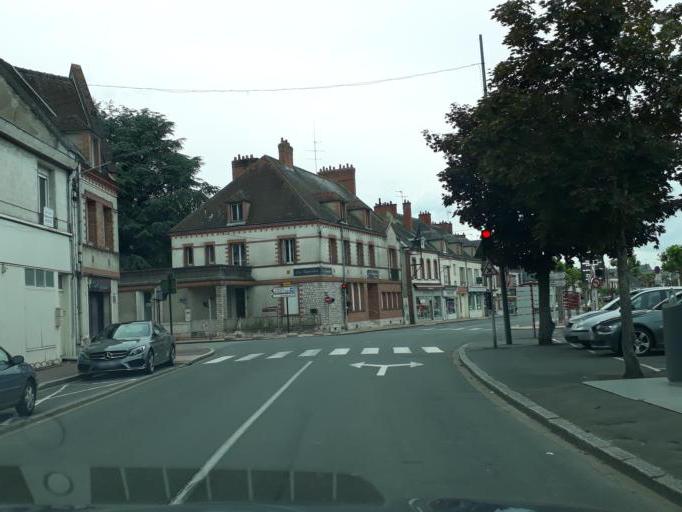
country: FR
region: Centre
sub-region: Departement du Loiret
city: Sully-sur-Loire
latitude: 47.7646
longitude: 2.3756
